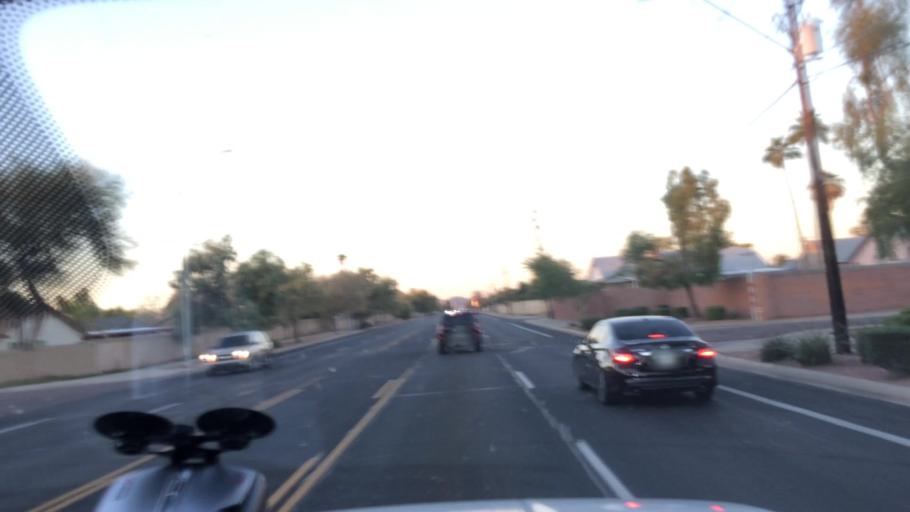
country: US
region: Arizona
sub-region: Maricopa County
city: Glendale
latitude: 33.6559
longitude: -112.0828
